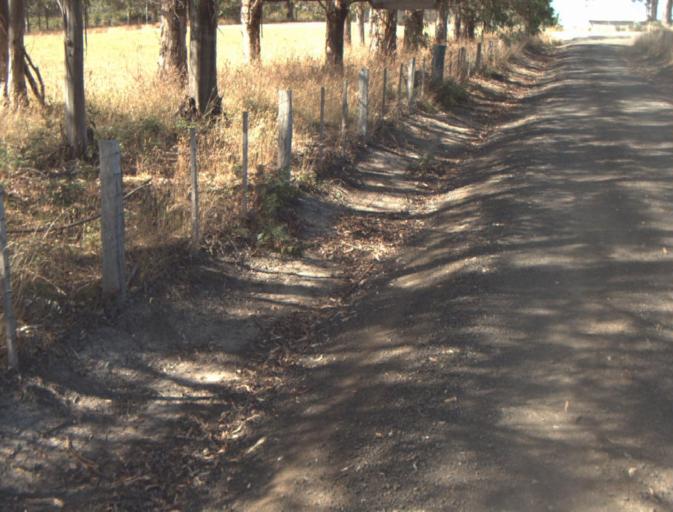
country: AU
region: Tasmania
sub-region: Launceston
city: Mayfield
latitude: -41.2066
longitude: 147.2180
